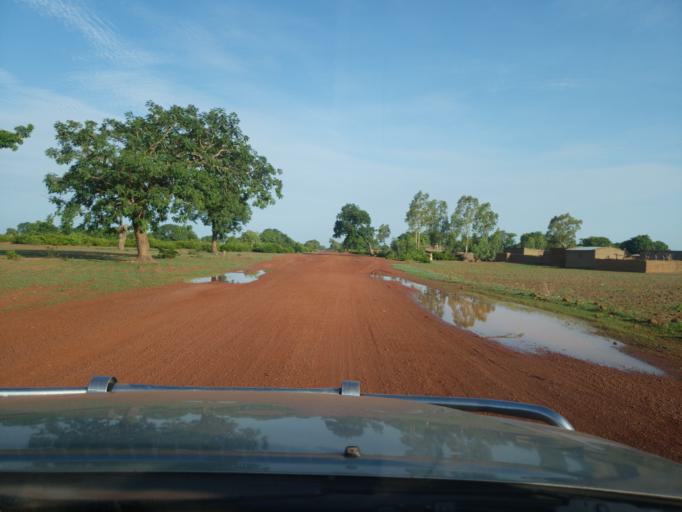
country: ML
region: Sikasso
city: Koutiala
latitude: 12.4172
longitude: -5.5732
